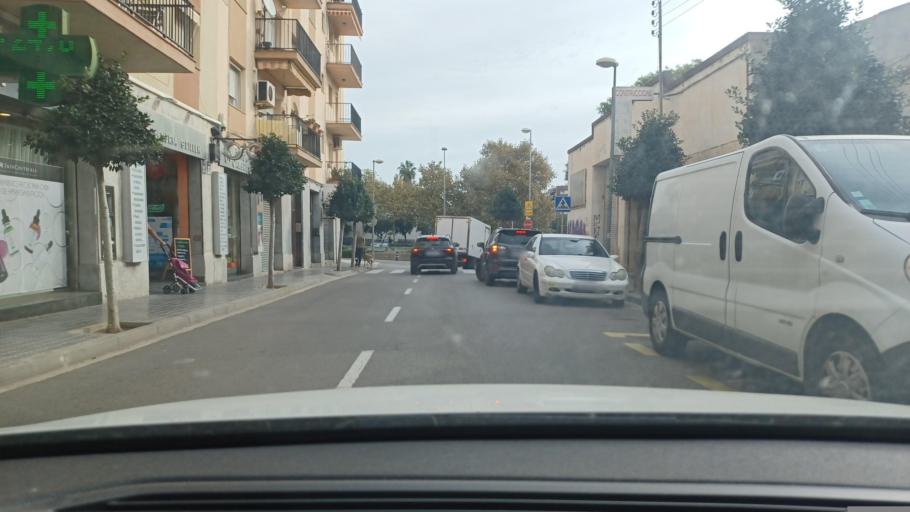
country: ES
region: Catalonia
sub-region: Provincia de Tarragona
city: Cambrils
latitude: 41.0696
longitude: 1.0550
